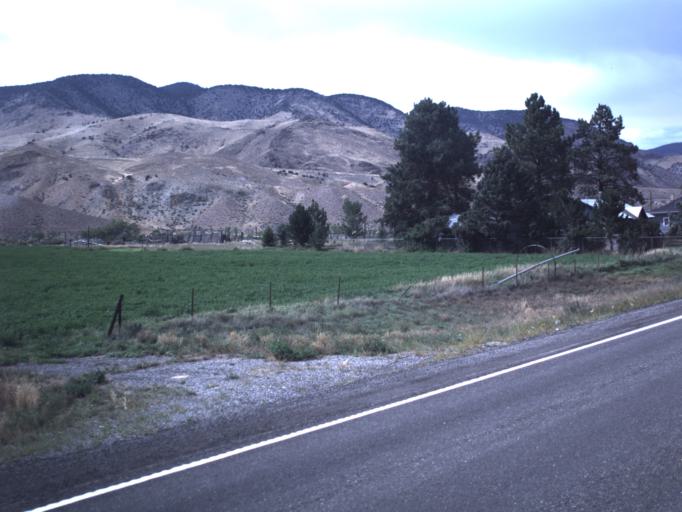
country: US
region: Utah
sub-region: Sevier County
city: Monroe
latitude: 38.4653
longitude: -112.2341
